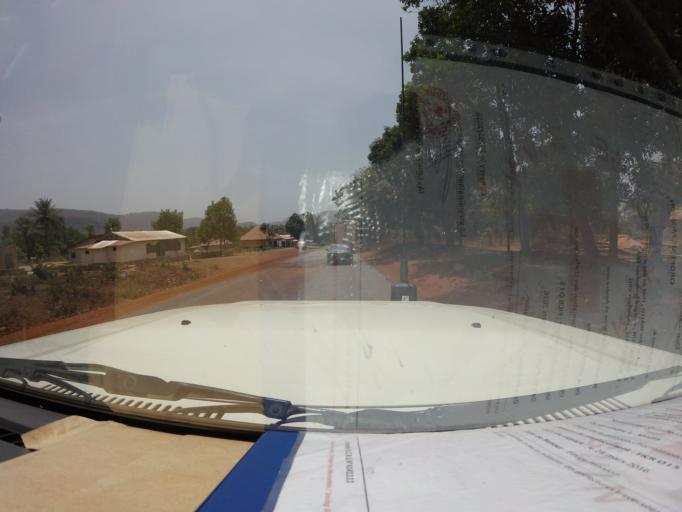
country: GN
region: Kindia
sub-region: Coyah
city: Coyah
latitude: 9.7974
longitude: -13.2913
